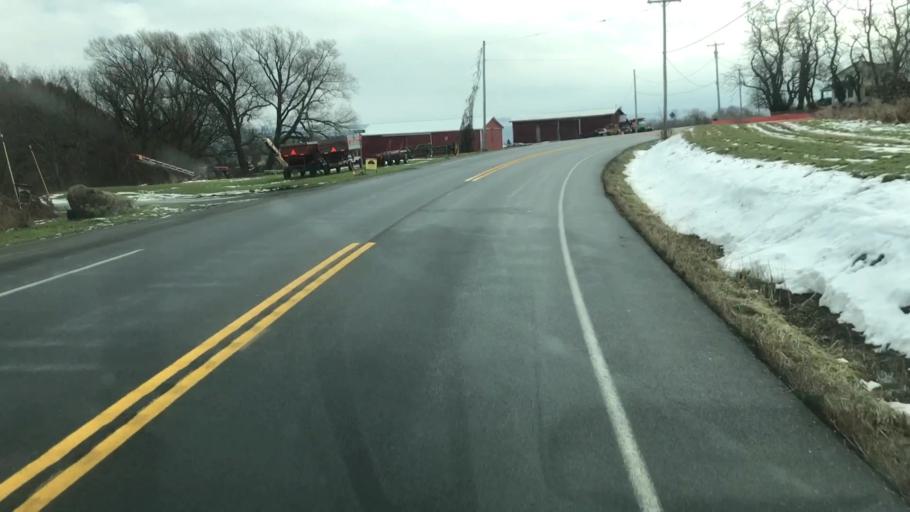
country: US
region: New York
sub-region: Onondaga County
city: Skaneateles
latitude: 42.8392
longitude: -76.3688
